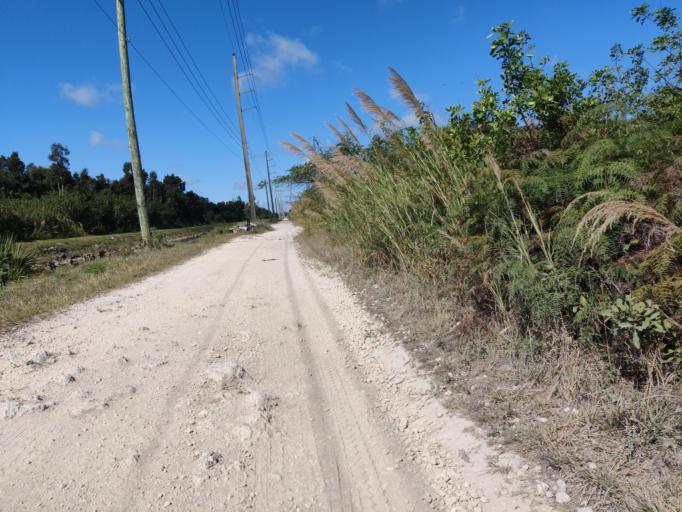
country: US
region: Florida
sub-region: Miami-Dade County
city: Kendall West
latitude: 25.7274
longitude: -80.4668
